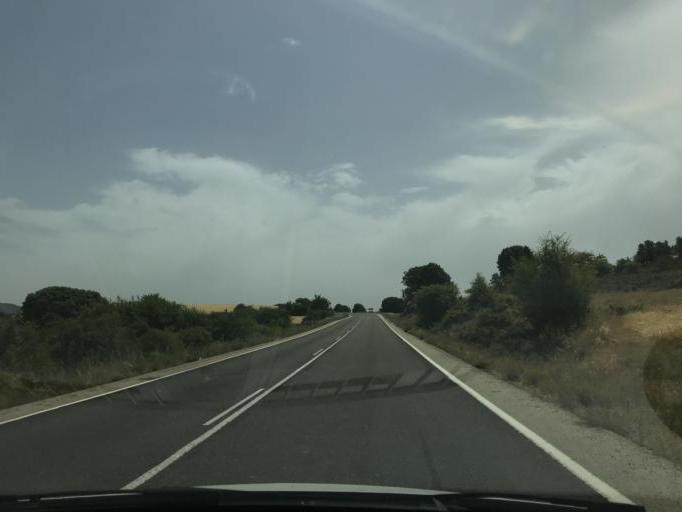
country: ES
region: Castille-La Mancha
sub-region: Provincia de Cuenca
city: La Frontera
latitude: 40.4017
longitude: -2.2394
